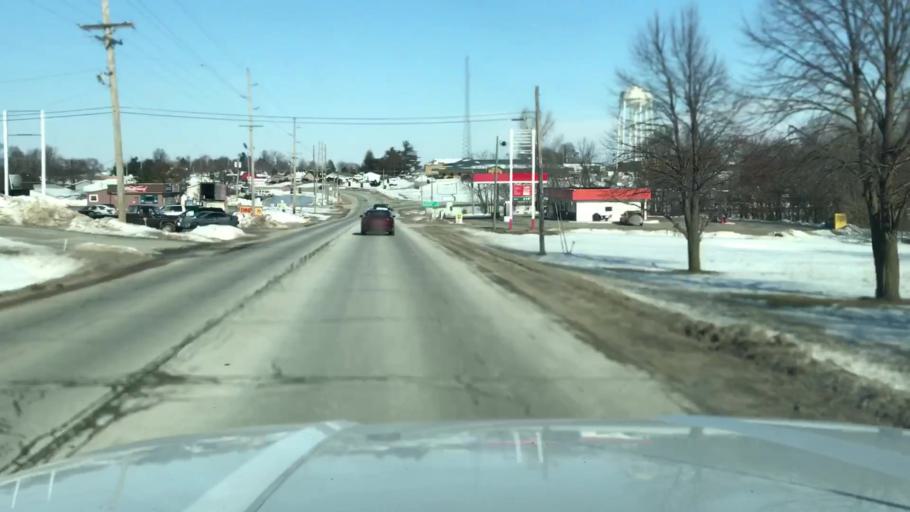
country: US
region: Missouri
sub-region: Andrew County
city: Savannah
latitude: 39.9428
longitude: -94.8219
